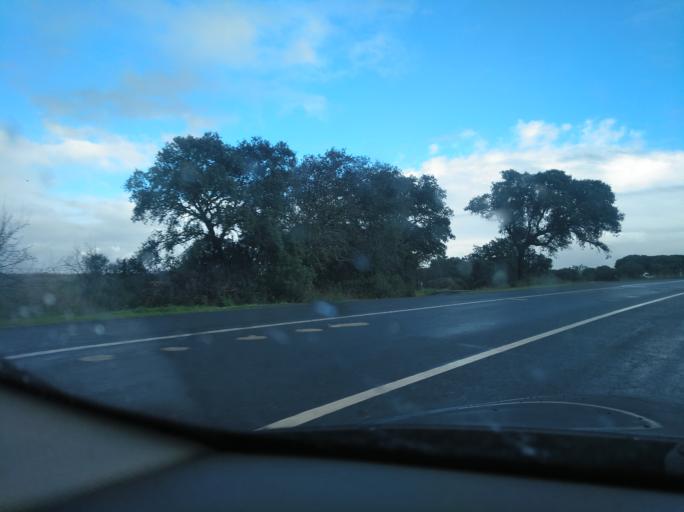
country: PT
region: Setubal
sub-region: Grandola
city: Grandola
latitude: 38.0104
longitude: -8.3802
